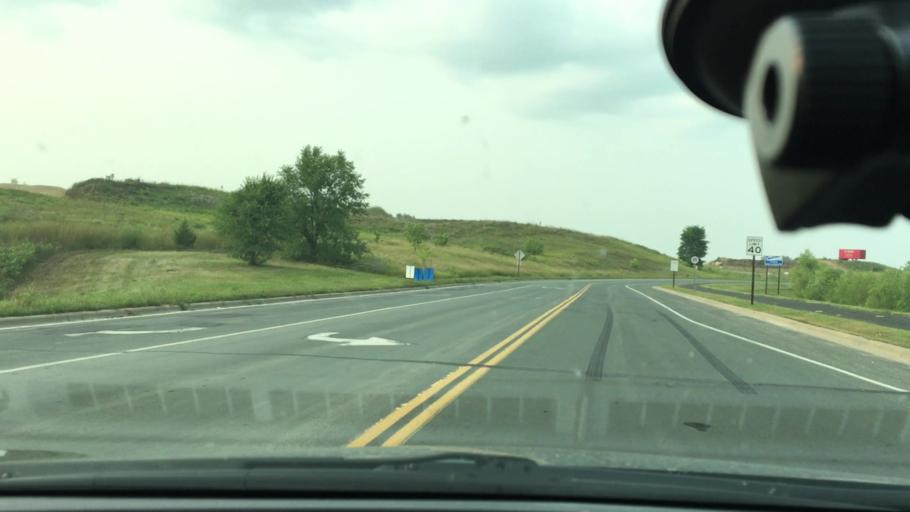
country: US
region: Minnesota
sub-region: Wright County
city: Otsego
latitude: 45.2531
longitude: -93.5647
